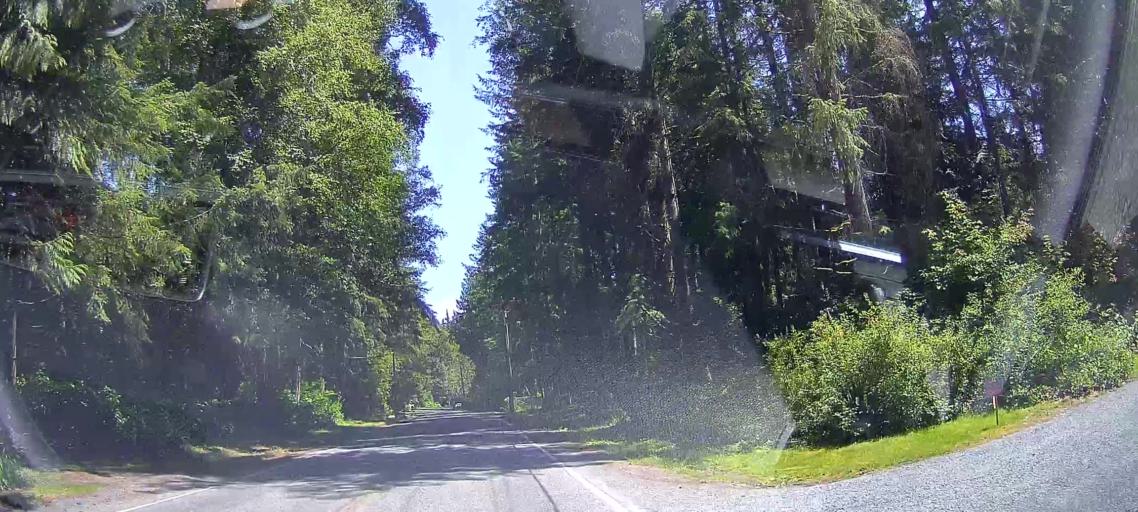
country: US
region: Washington
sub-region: Skagit County
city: Burlington
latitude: 48.5932
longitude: -122.3213
